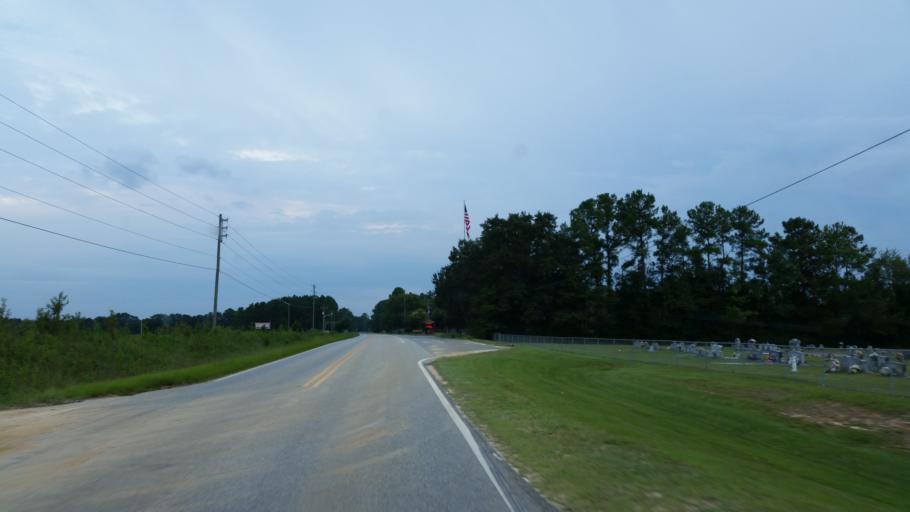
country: US
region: Georgia
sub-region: Lowndes County
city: Valdosta
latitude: 30.7239
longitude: -83.3183
